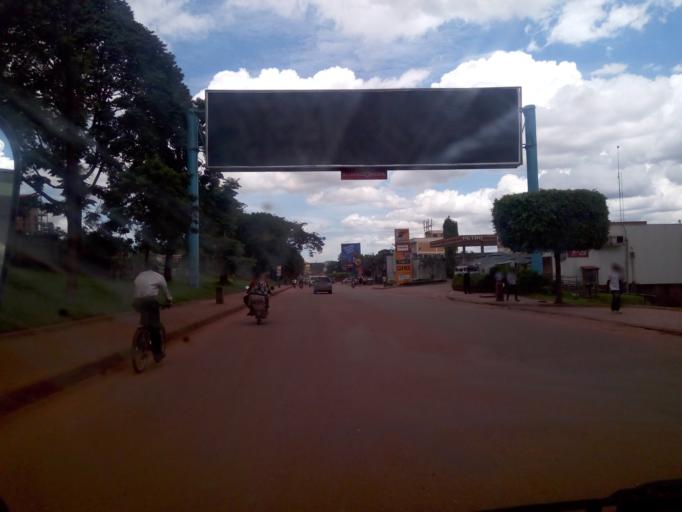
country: UG
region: Central Region
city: Kampala Central Division
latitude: 0.3238
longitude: 32.5741
